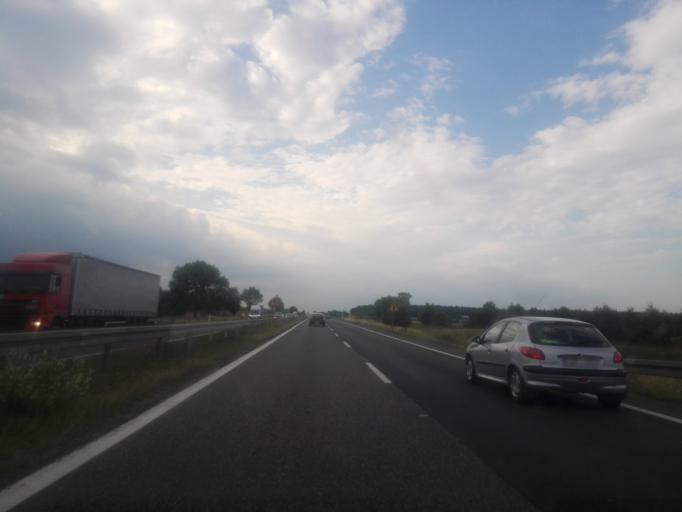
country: PL
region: Silesian Voivodeship
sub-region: Powiat myszkowski
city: Kozieglowy
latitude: 50.5513
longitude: 19.1791
